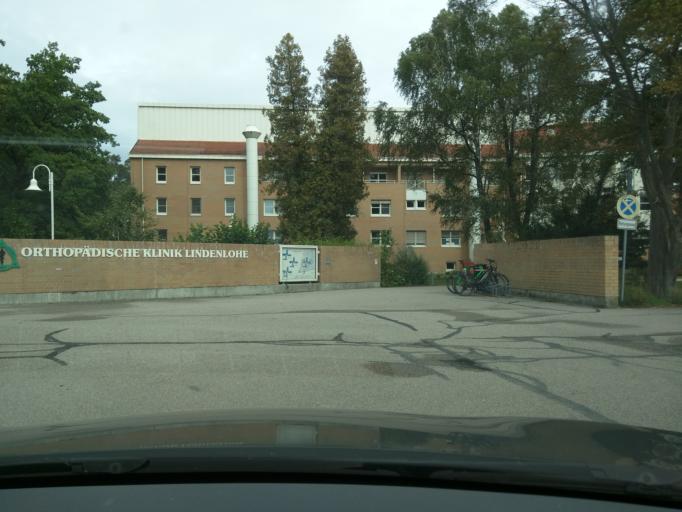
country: DE
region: Bavaria
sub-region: Upper Palatinate
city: Schwarzenfeld
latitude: 49.3586
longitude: 12.1572
